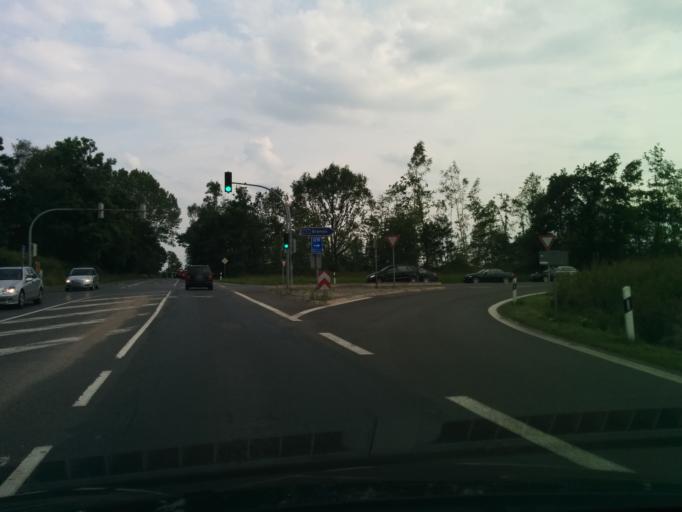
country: DE
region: Lower Saxony
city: Seevetal
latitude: 53.3821
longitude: 9.9799
